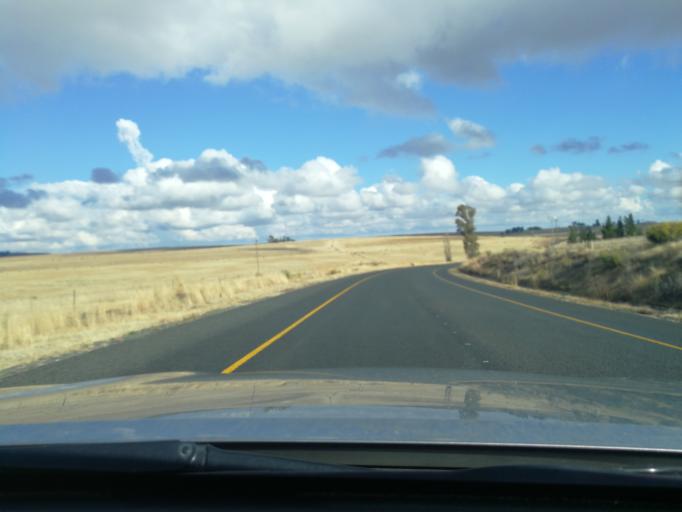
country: ZA
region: Orange Free State
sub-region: Thabo Mofutsanyana District Municipality
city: Reitz
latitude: -27.9029
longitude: 28.3961
